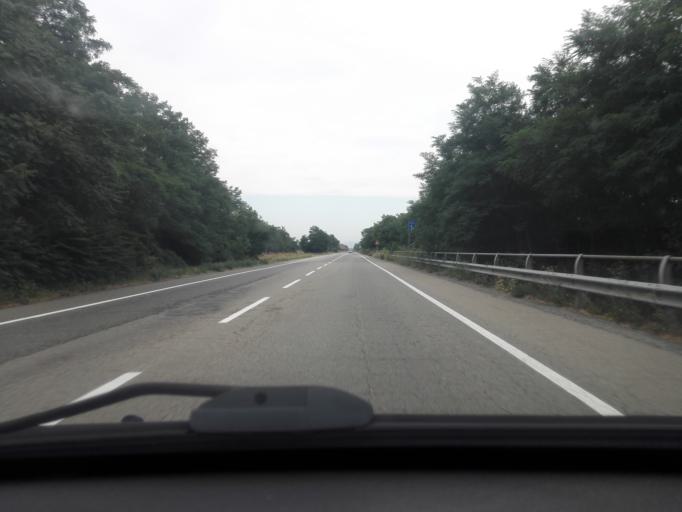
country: IT
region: Piedmont
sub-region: Provincia di Alessandria
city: Litta Parodi-Cascinagrossa
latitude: 44.8484
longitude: 8.7218
